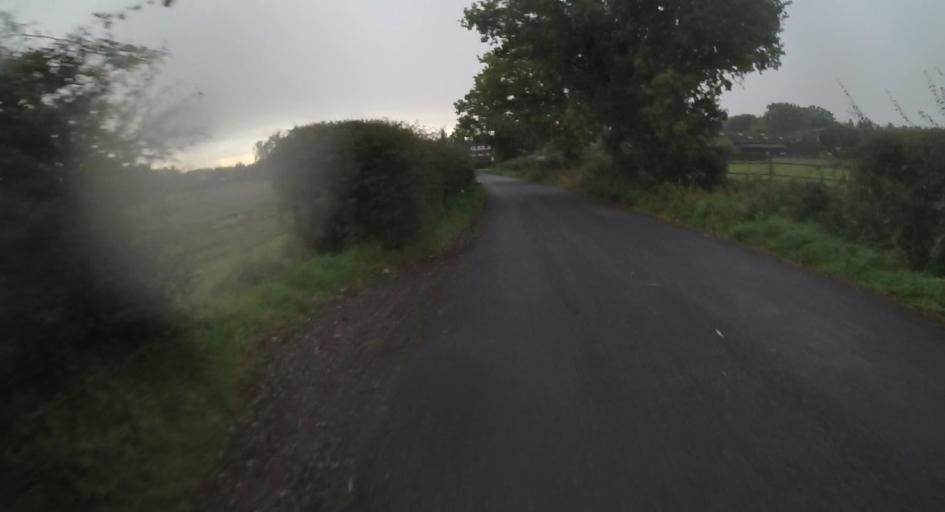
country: GB
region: England
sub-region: Hampshire
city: Tadley
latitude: 51.3181
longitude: -1.1485
